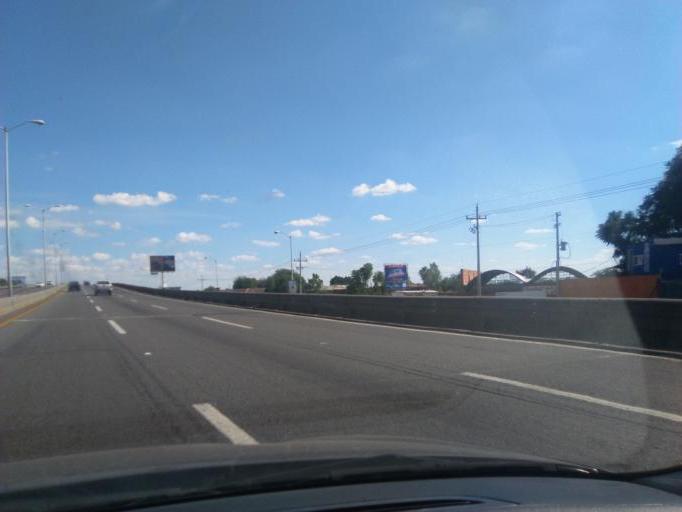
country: MX
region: Guanajuato
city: Silao
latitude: 20.9613
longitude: -101.4497
